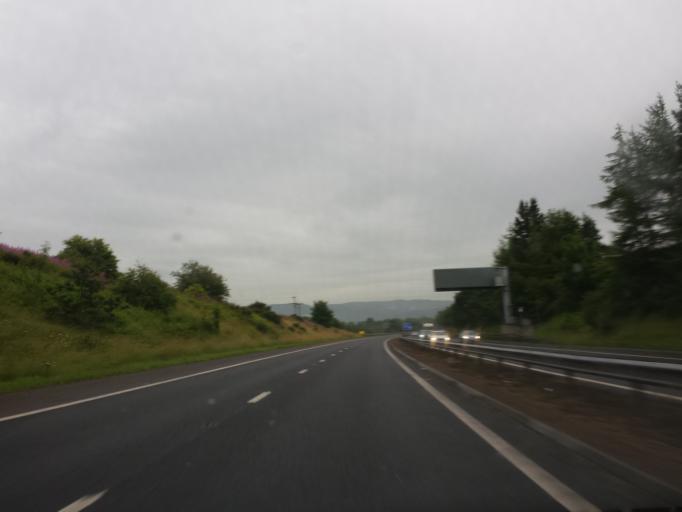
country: GB
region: Scotland
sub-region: Perth and Kinross
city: Bridge of Earn
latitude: 56.3579
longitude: -3.4043
